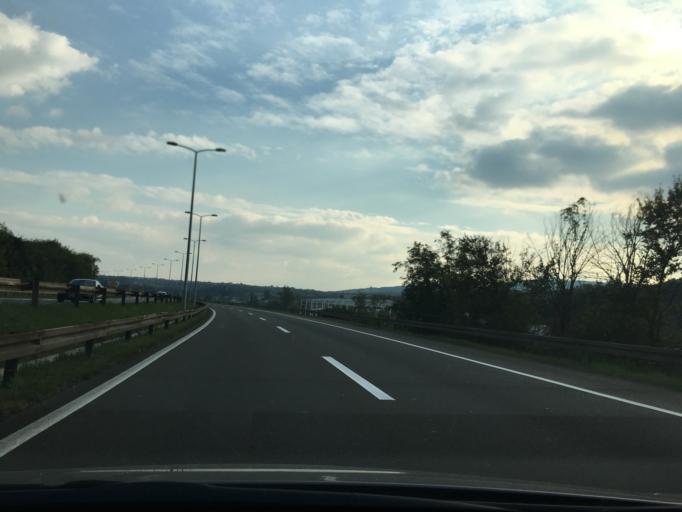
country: RS
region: Central Serbia
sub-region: Belgrade
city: Zvezdara
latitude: 44.7296
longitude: 20.5391
